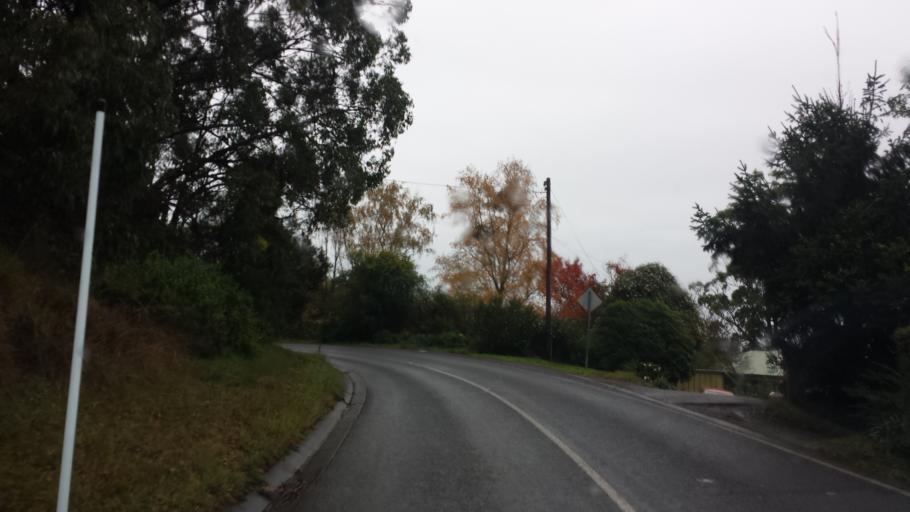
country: AU
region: Victoria
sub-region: Yarra Ranges
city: Monbulk
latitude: -37.8933
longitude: 145.3972
